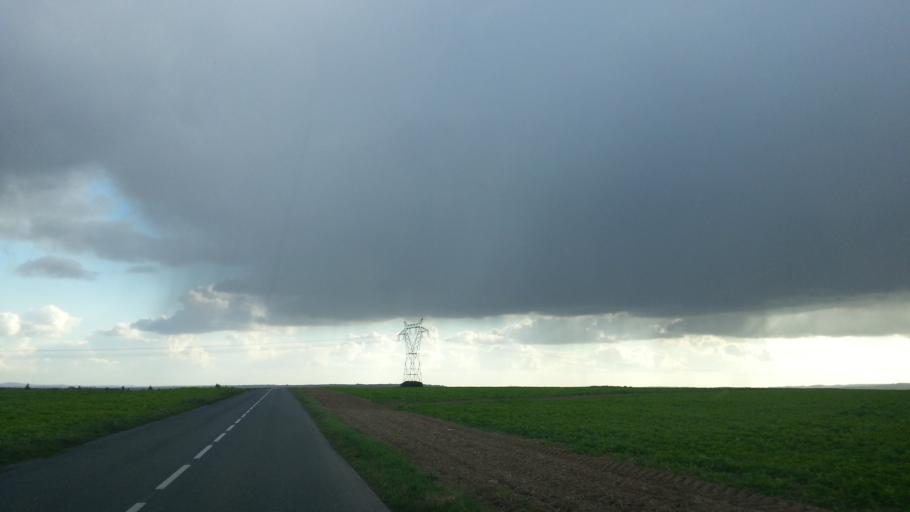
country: FR
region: Picardie
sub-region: Departement de l'Oise
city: Villers-sous-Saint-Leu
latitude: 49.2333
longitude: 2.4109
